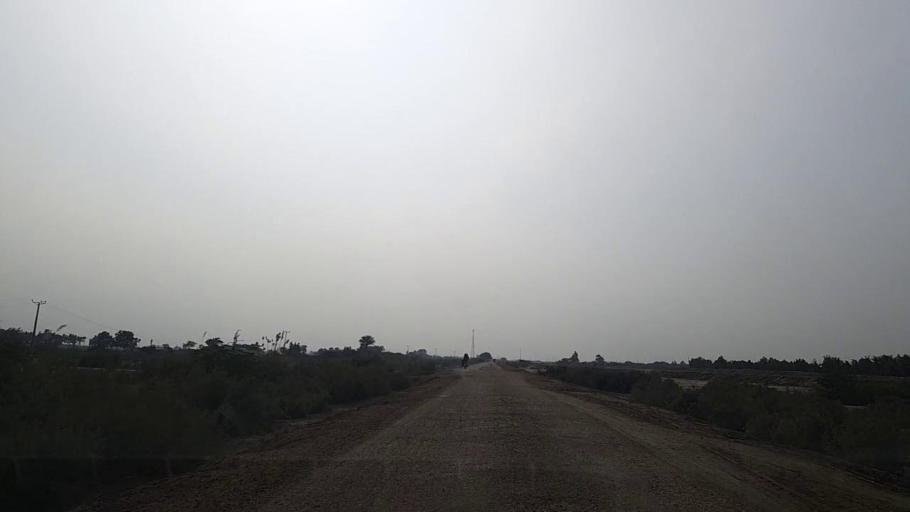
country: PK
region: Sindh
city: Mirpur Sakro
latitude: 24.6424
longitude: 67.6029
